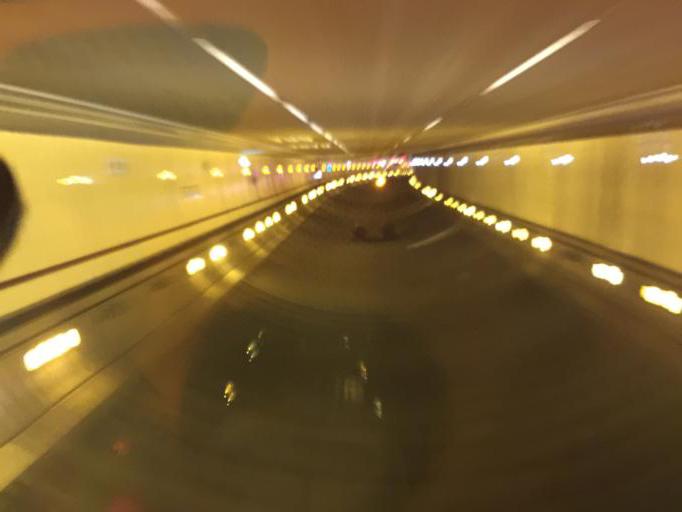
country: ES
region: Andalusia
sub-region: Provincia de Malaga
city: Malaga
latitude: 36.7569
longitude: -4.4217
